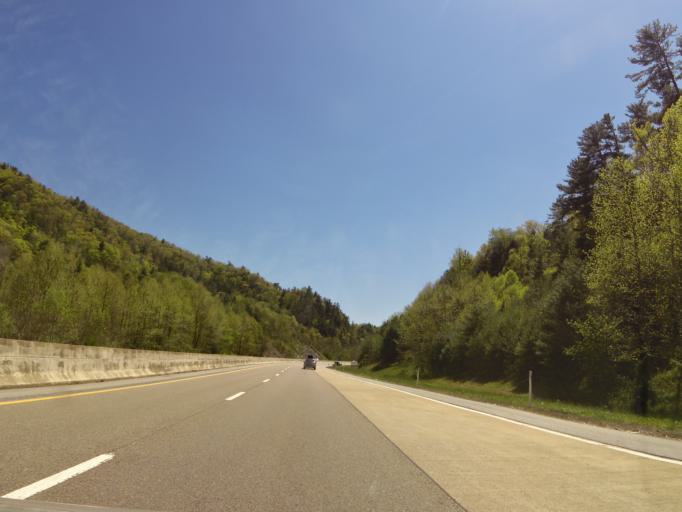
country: US
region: Tennessee
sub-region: Unicoi County
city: Banner Hill
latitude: 36.0833
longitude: -82.4948
